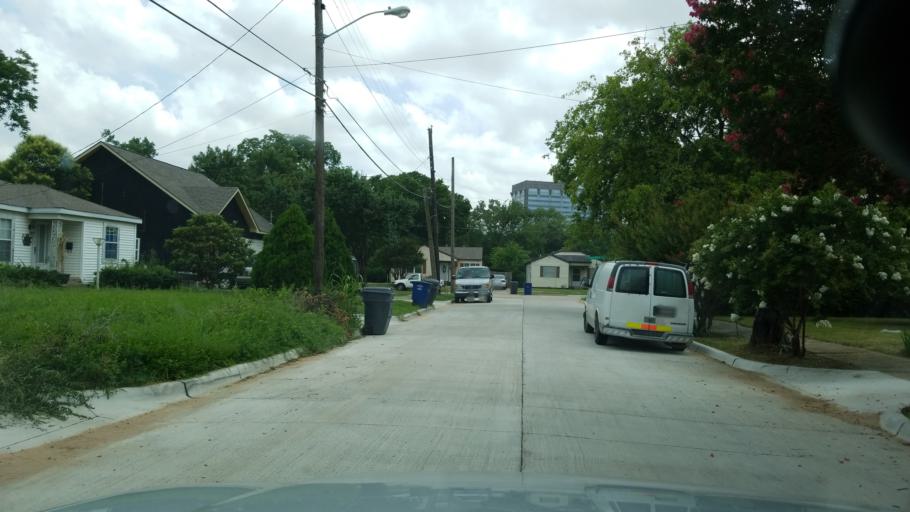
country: US
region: Texas
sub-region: Dallas County
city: Dallas
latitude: 32.8155
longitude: -96.8587
